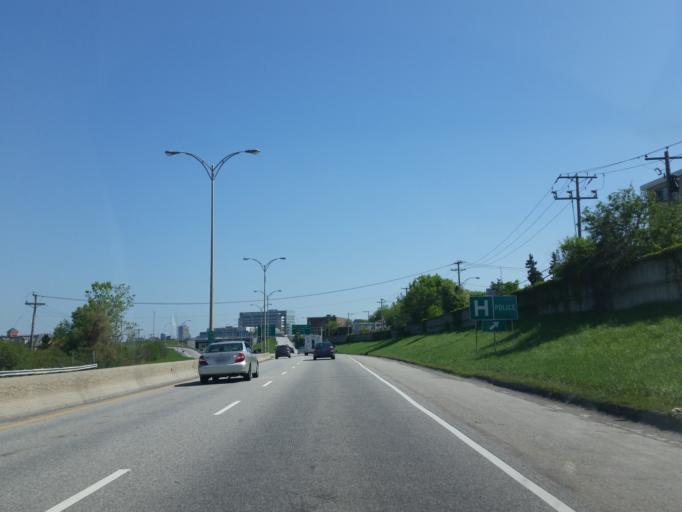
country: CA
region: Quebec
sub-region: Outaouais
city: Gatineau
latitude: 45.4525
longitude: -75.7353
